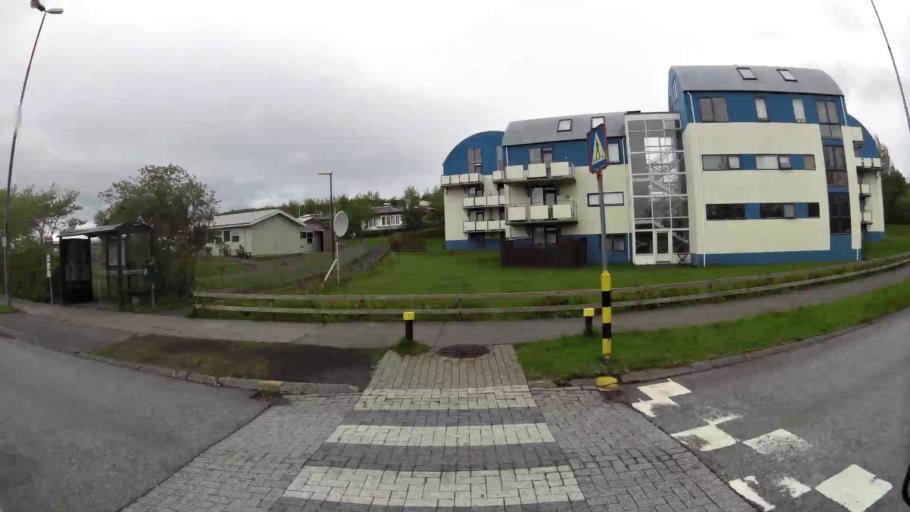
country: IS
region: Capital Region
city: Hafnarfjoerdur
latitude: 64.0659
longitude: -21.9333
